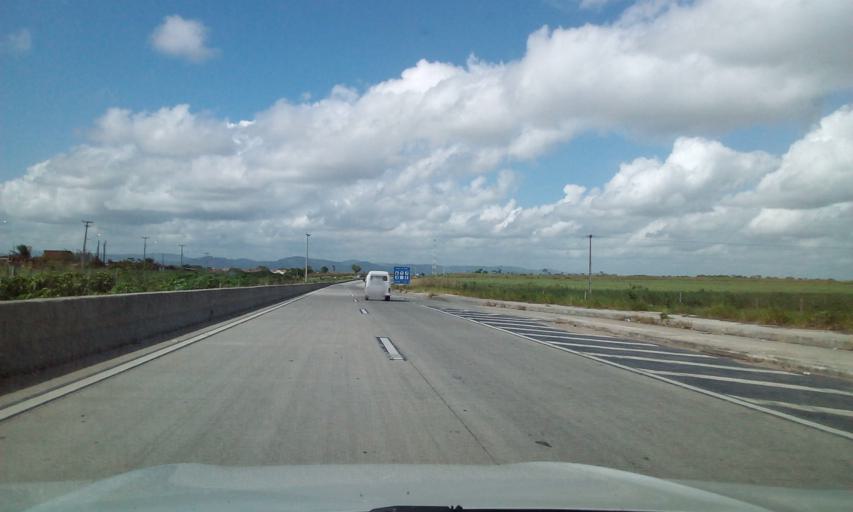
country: BR
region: Alagoas
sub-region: Messias
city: Messias
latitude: -9.3972
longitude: -35.8364
